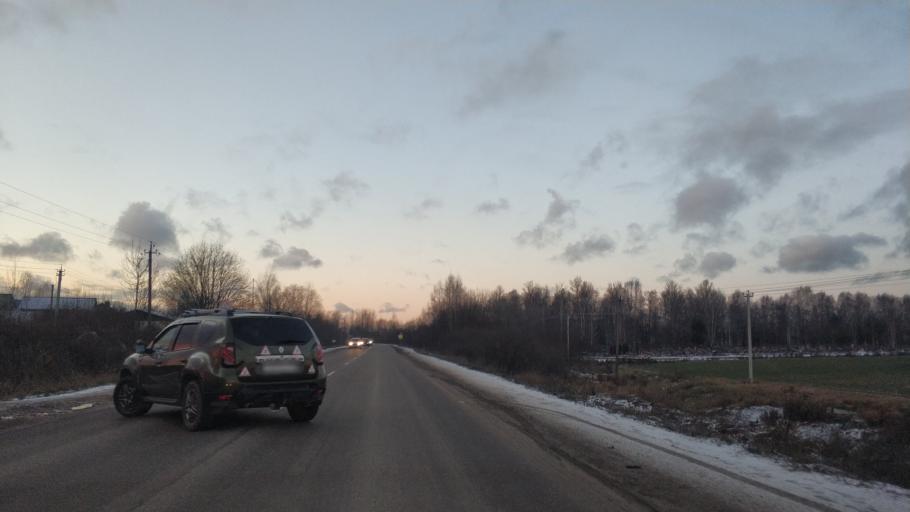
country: RU
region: St.-Petersburg
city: Pontonnyy
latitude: 59.8051
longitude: 30.6253
